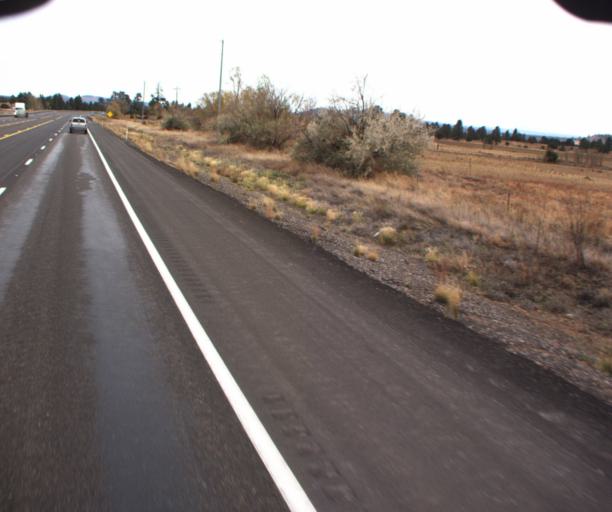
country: US
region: Arizona
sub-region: Coconino County
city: Flagstaff
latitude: 35.3367
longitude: -111.5528
